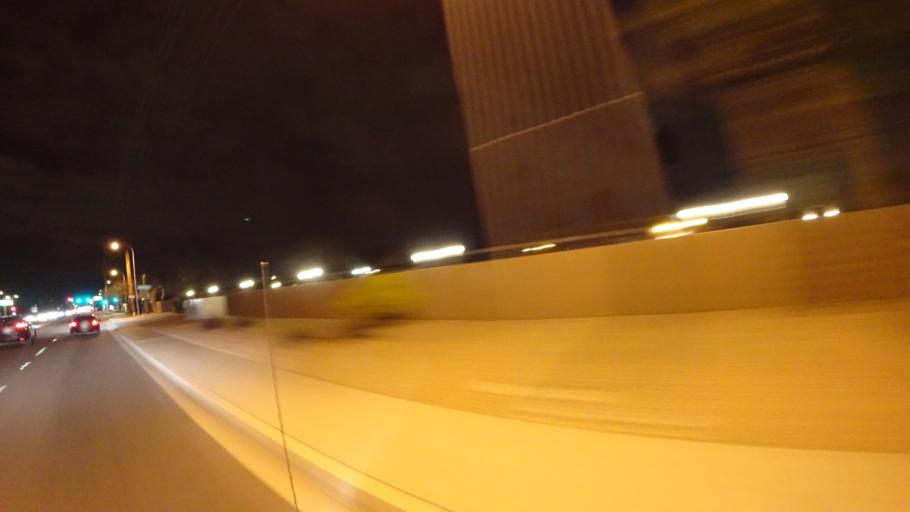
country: US
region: Arizona
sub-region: Maricopa County
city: Tempe
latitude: 33.4204
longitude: -111.9090
